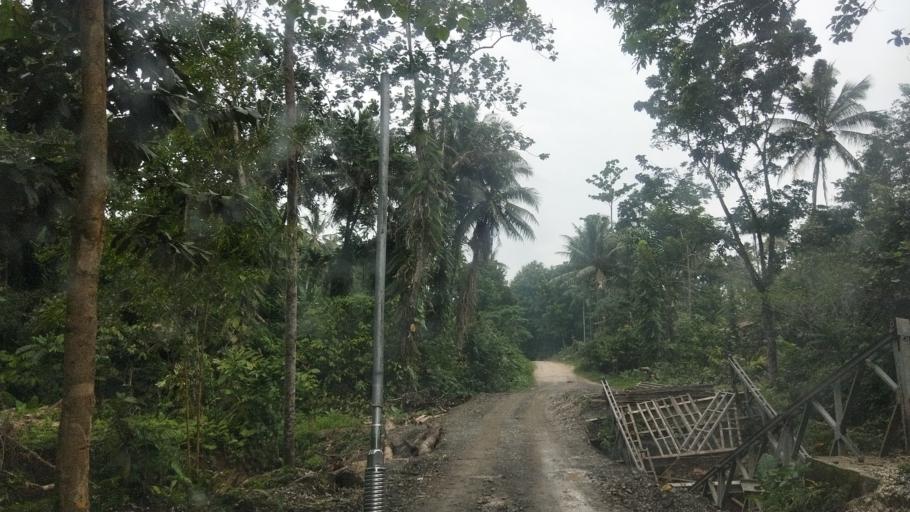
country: SB
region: Malaita
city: Auki
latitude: -8.9744
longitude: 160.7833
